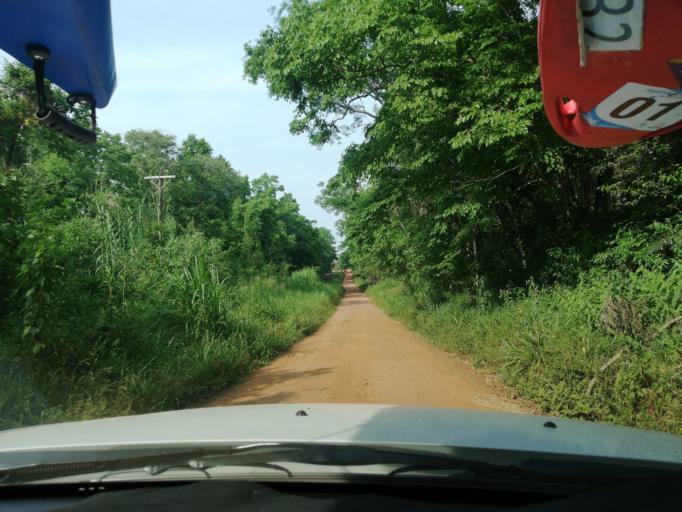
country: AR
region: Misiones
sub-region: Departamento de San Ignacio
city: San Ignacio
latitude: -27.2979
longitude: -55.5728
